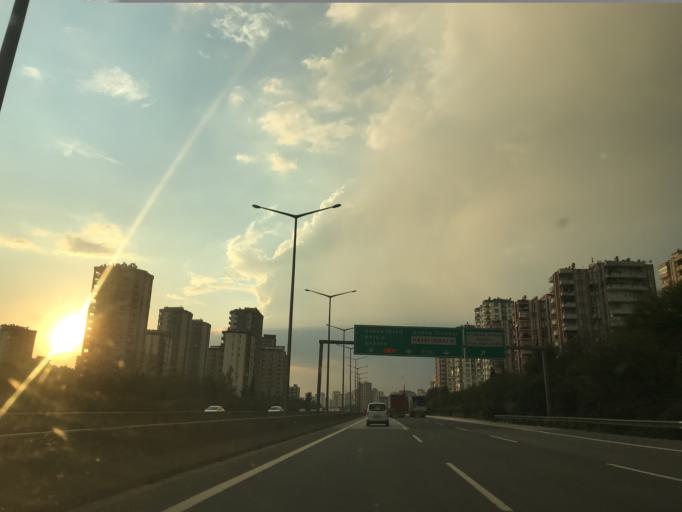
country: TR
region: Adana
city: Seyhan
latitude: 37.0315
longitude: 35.2627
